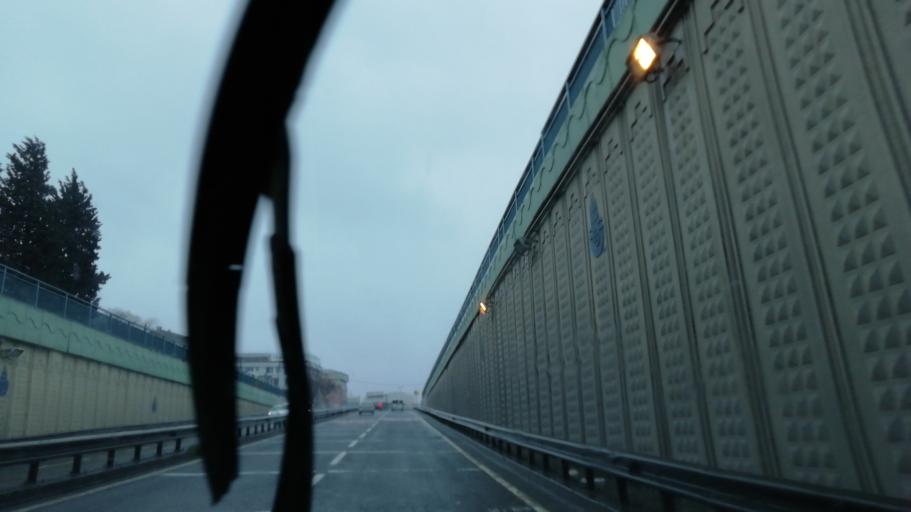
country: TR
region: Istanbul
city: Yakuplu
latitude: 40.9892
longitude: 28.7208
